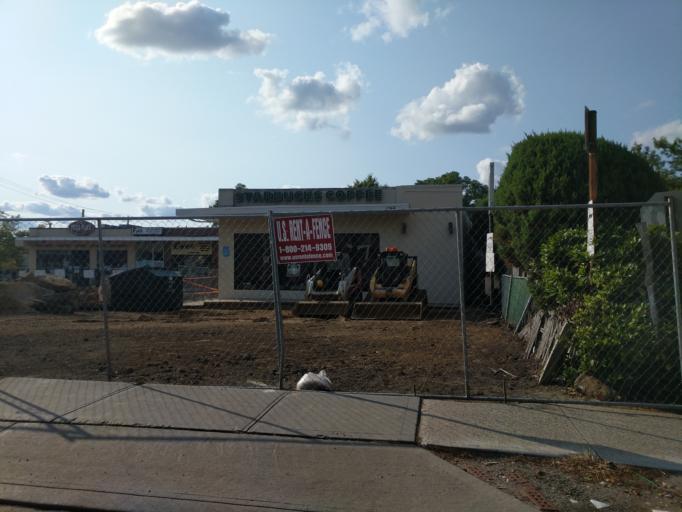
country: US
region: New York
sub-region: Nassau County
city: Hewlett
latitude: 40.6406
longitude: -73.6992
